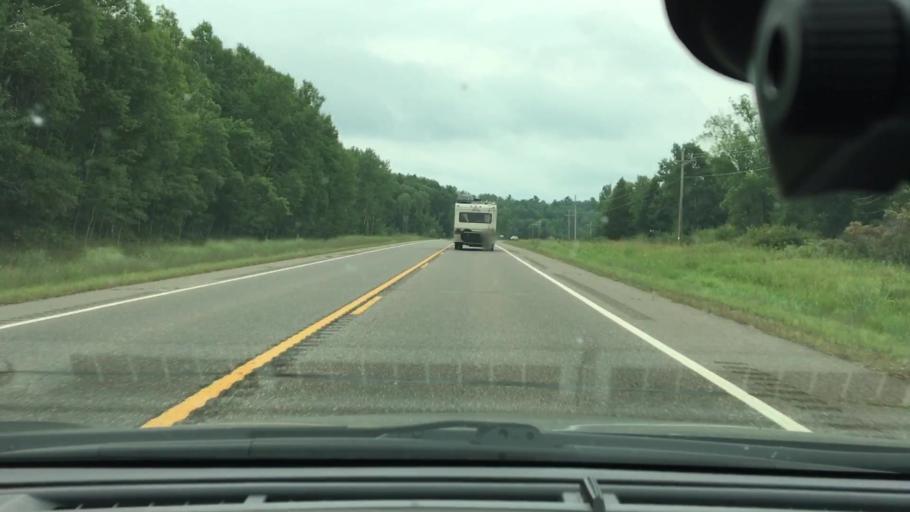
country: US
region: Minnesota
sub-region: Crow Wing County
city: Crosby
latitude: 46.5065
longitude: -93.9590
